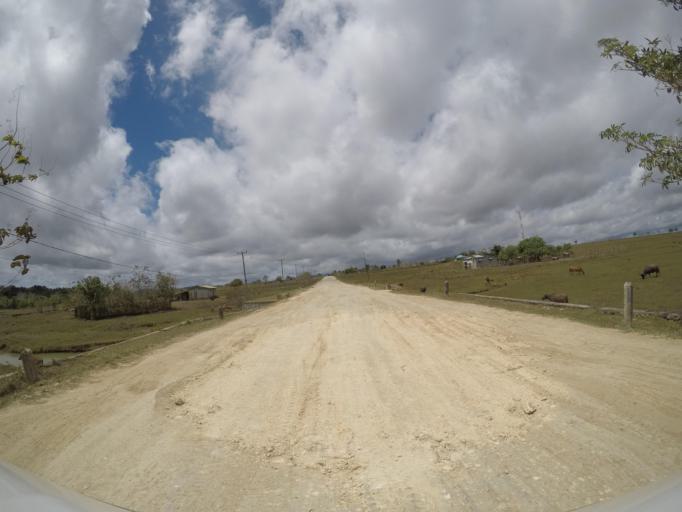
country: TL
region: Lautem
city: Lospalos
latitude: -8.4402
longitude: 126.9852
